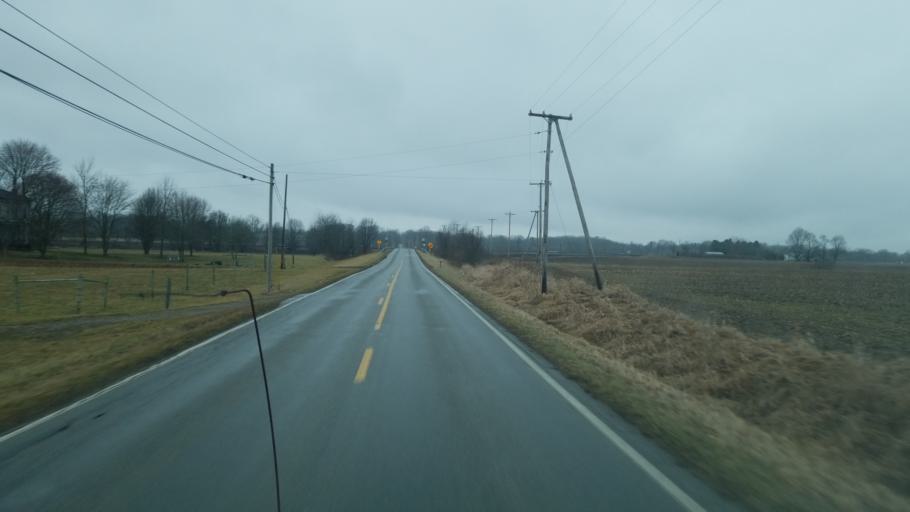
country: US
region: Ohio
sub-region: Wayne County
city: Smithville
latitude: 40.8589
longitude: -81.8375
